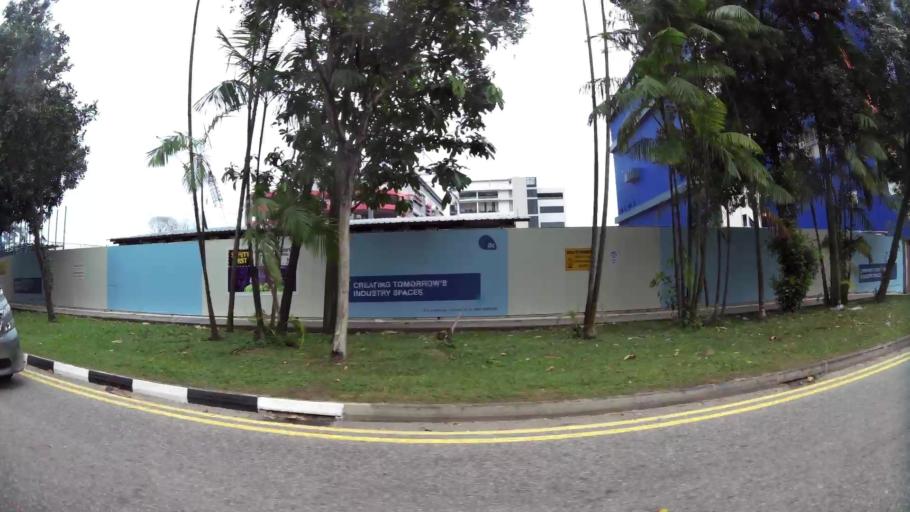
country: SG
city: Singapore
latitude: 1.3138
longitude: 103.7227
